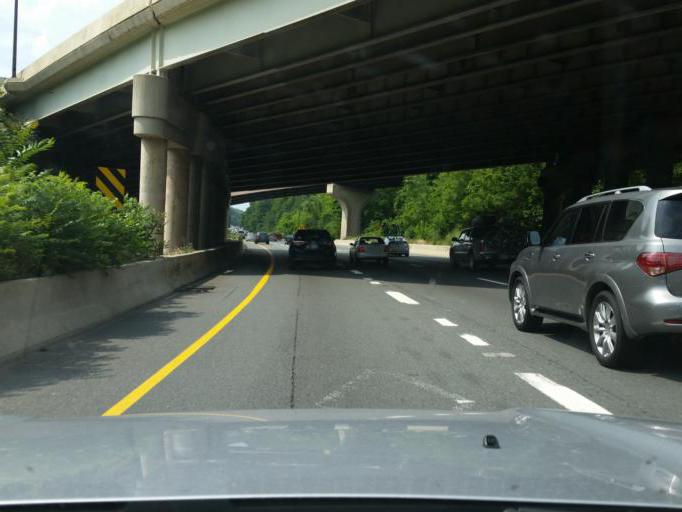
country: US
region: Maryland
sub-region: Montgomery County
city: North Bethesda
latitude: 39.0330
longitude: -77.1421
